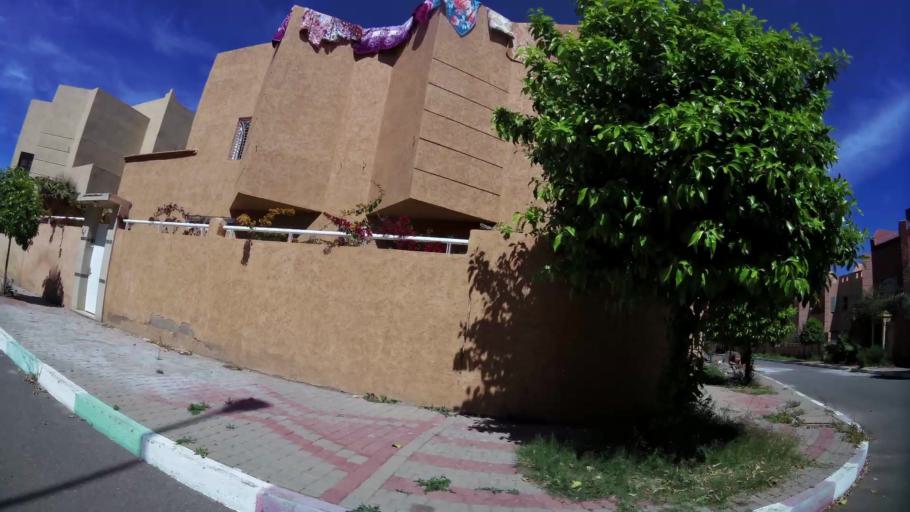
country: MA
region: Marrakech-Tensift-Al Haouz
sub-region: Marrakech
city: Marrakesh
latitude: 31.6365
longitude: -8.1084
